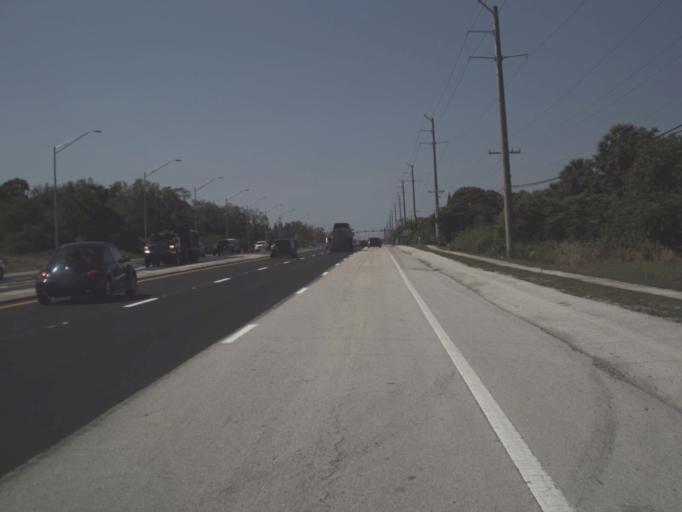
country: US
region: Florida
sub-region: Brevard County
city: South Patrick Shores
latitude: 28.1685
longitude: -80.6454
